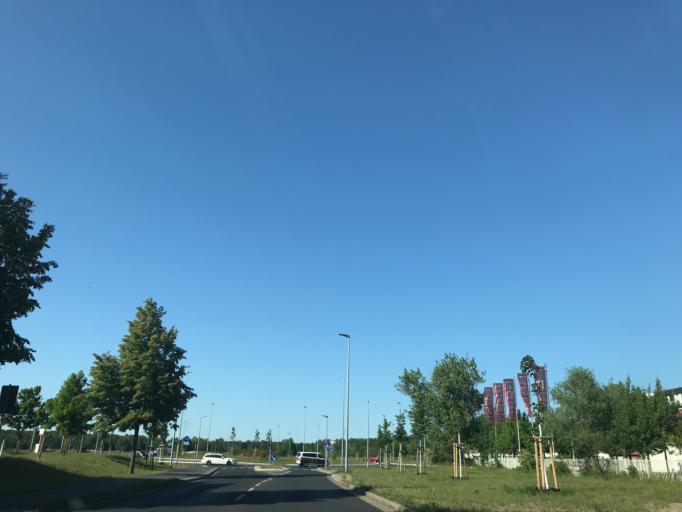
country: DE
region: Brandenburg
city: Falkensee
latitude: 52.5598
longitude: 13.1252
